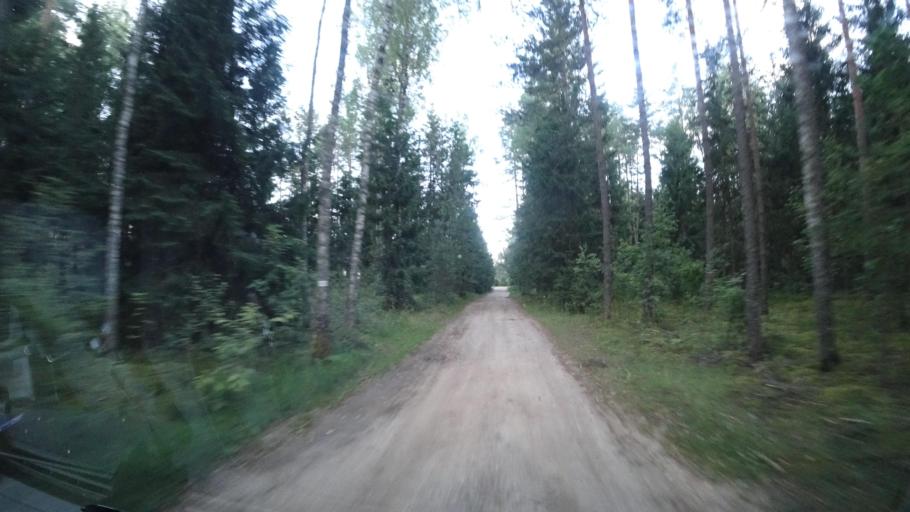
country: LT
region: Vilnius County
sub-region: Trakai
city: Rudiskes
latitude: 54.5089
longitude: 24.8894
